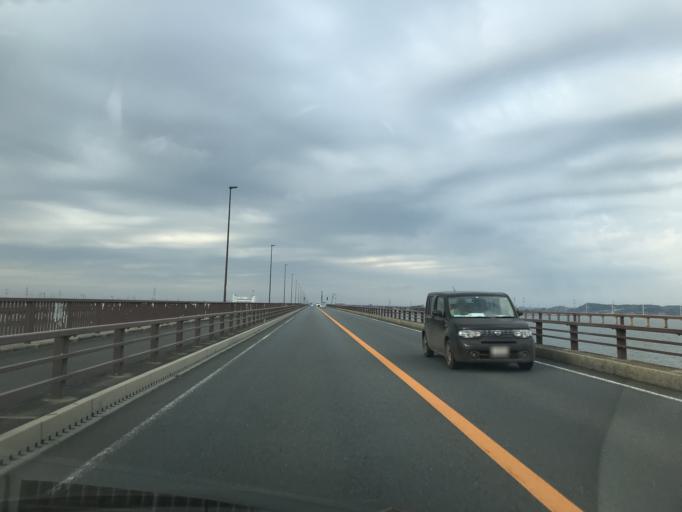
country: JP
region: Ibaraki
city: Kashima-shi
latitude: 35.9641
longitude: 140.6091
